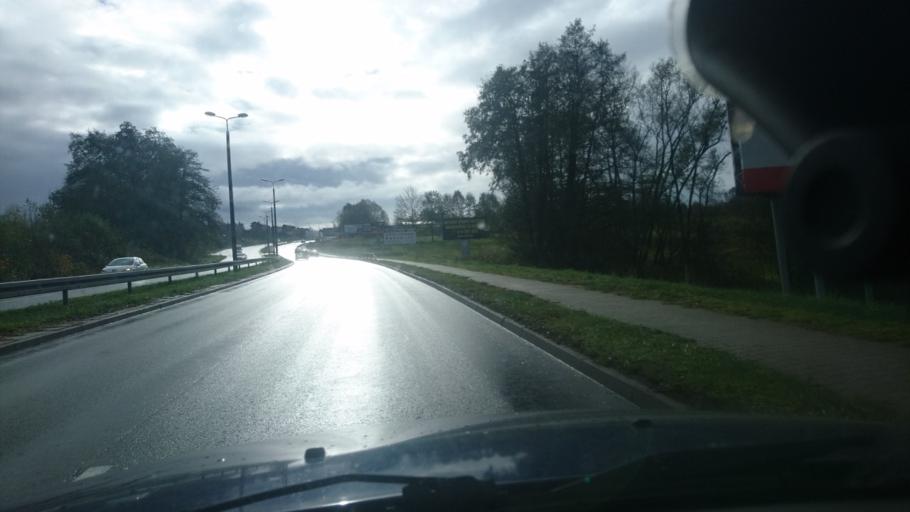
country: PL
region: Silesian Voivodeship
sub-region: Bielsko-Biala
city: Bielsko-Biala
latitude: 49.8329
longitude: 19.0098
